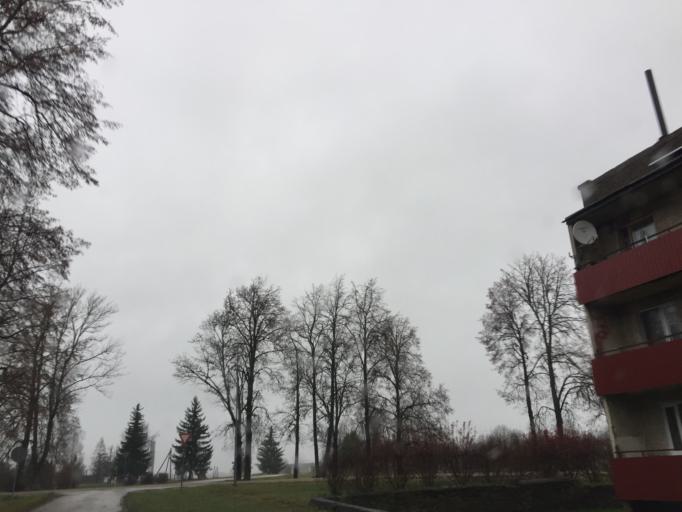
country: LV
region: Viesite
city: Viesite
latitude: 56.4583
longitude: 25.4860
